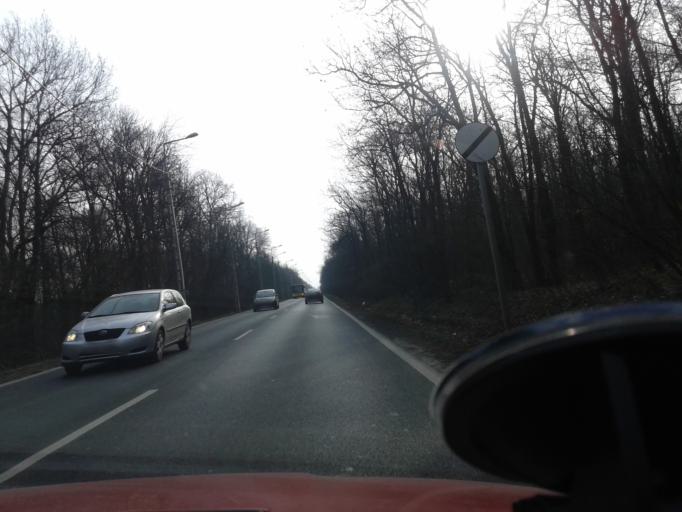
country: HU
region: Budapest
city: Budapest XXII. keruelet
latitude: 47.4412
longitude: 18.9996
